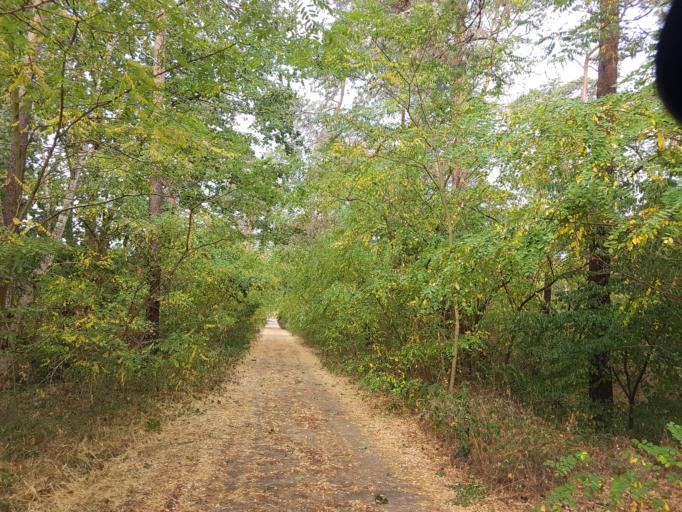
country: DE
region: Brandenburg
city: Finsterwalde
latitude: 51.6003
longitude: 13.7492
